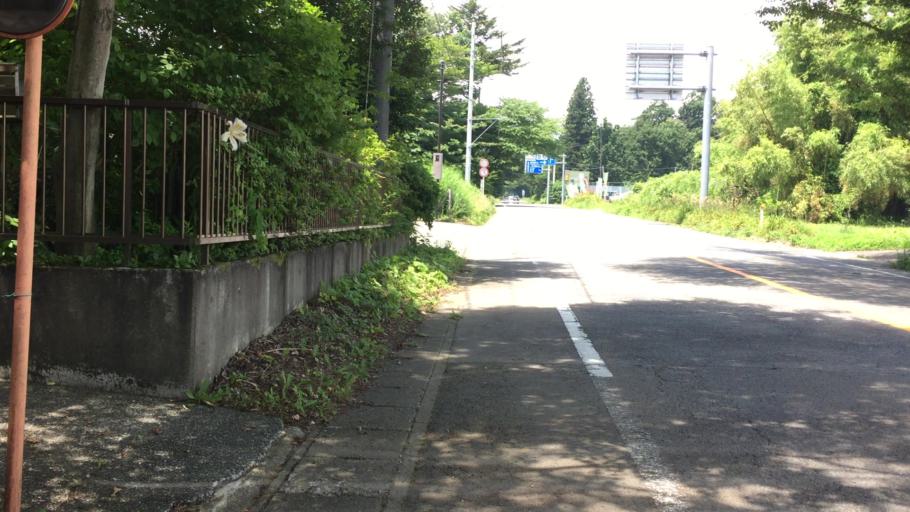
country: JP
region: Tochigi
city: Kuroiso
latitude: 37.0139
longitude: 139.9610
